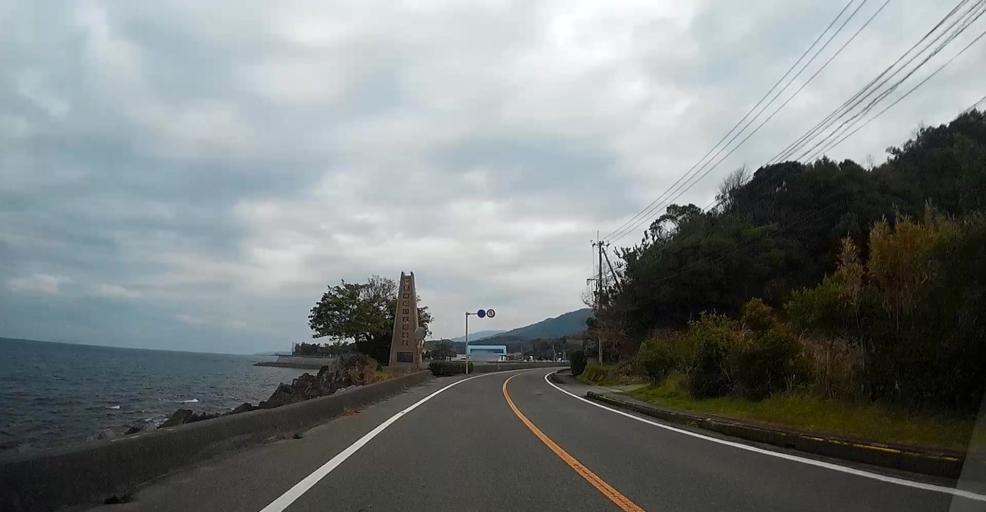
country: JP
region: Kumamoto
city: Hondo
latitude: 32.4602
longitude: 130.2266
